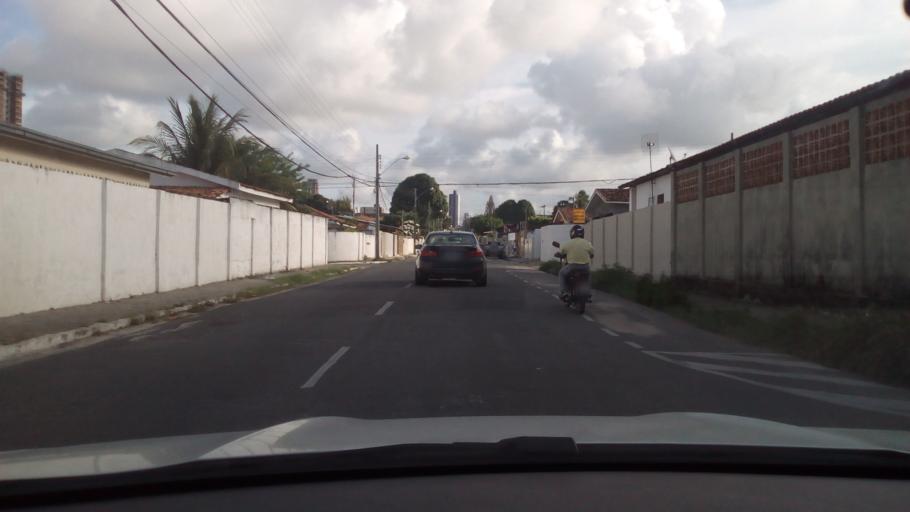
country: BR
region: Paraiba
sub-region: Joao Pessoa
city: Joao Pessoa
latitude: -7.1023
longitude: -34.8577
